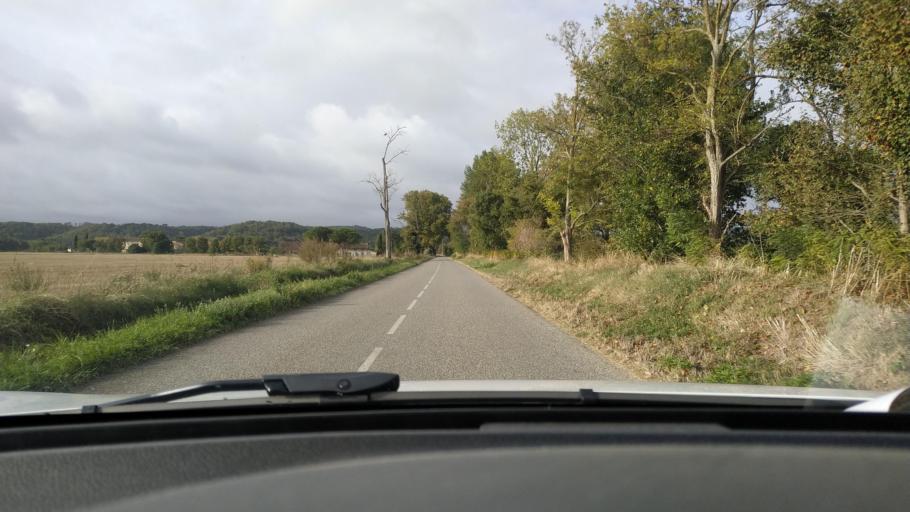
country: FR
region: Midi-Pyrenees
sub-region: Departement de la Haute-Garonne
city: Auterive
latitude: 43.3331
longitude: 1.4502
